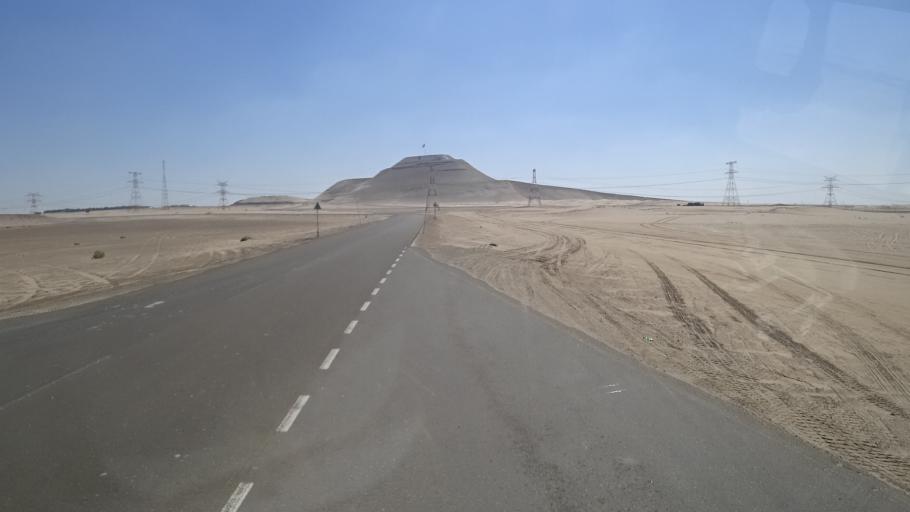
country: AE
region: Abu Dhabi
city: Abu Dhabi
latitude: 24.1755
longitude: 54.6960
